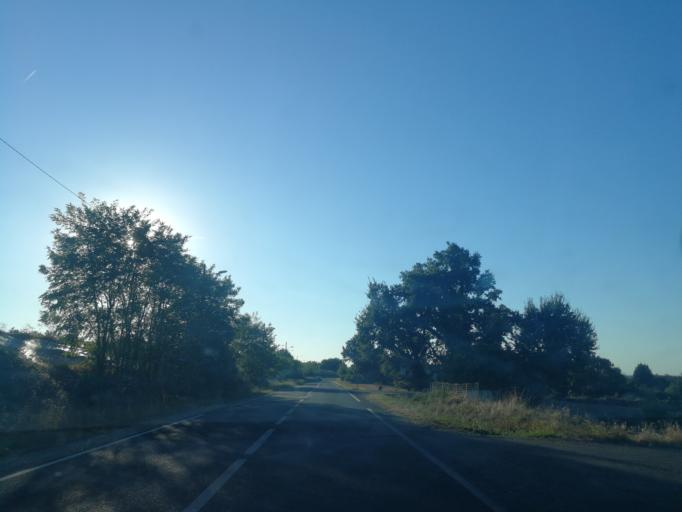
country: FR
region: Midi-Pyrenees
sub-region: Departement de la Haute-Garonne
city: Montrabe
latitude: 43.6328
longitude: 1.5062
